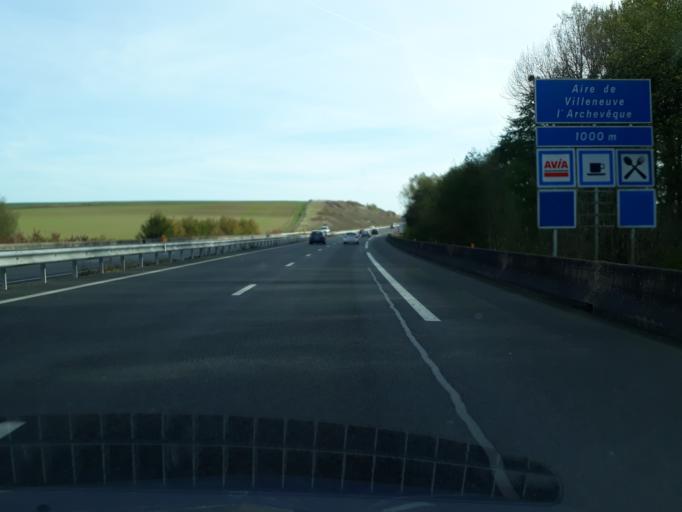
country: FR
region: Bourgogne
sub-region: Departement de l'Yonne
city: Thorigny-sur-Oreuse
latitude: 48.2480
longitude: 3.5347
